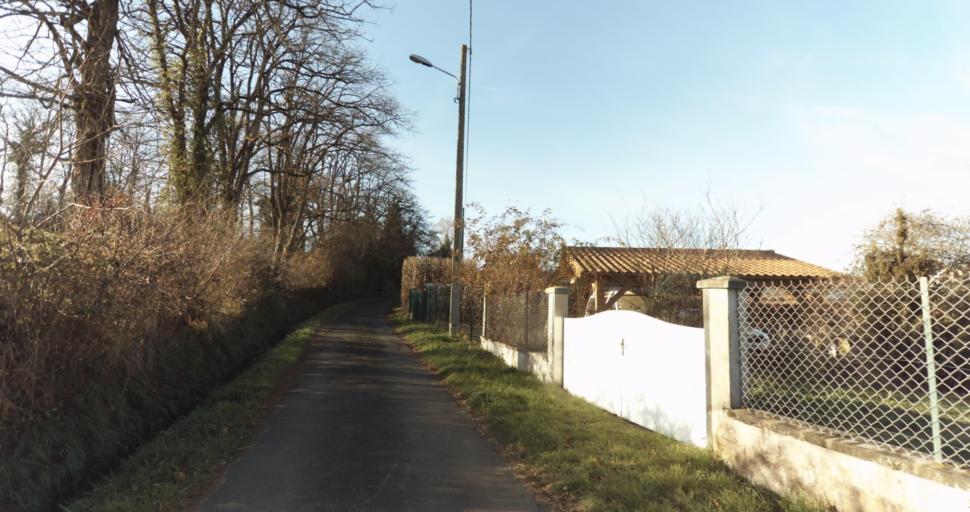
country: FR
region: Limousin
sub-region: Departement de la Haute-Vienne
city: Aixe-sur-Vienne
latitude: 45.7955
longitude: 1.1214
